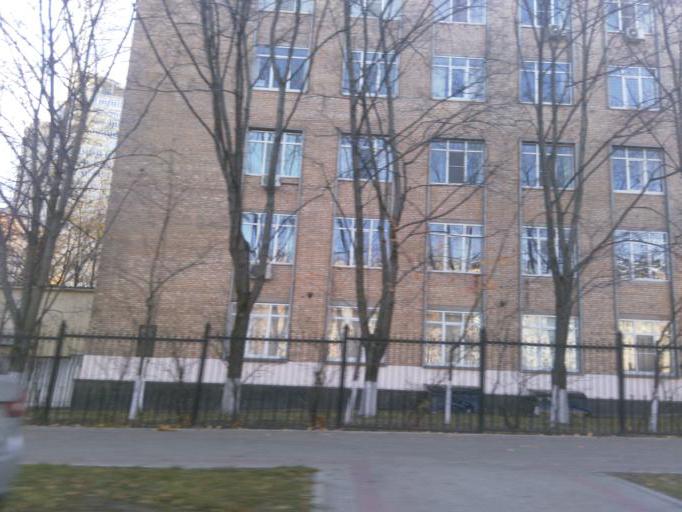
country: RU
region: Moskovskaya
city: Leninskiye Gory
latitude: 55.6961
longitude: 37.5603
